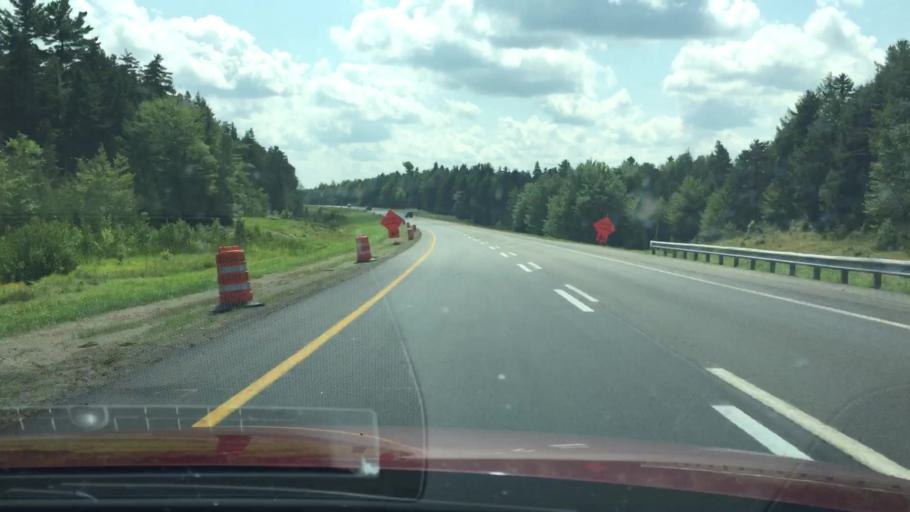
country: US
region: Maine
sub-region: Penobscot County
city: Medway
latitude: 45.6742
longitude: -68.4985
